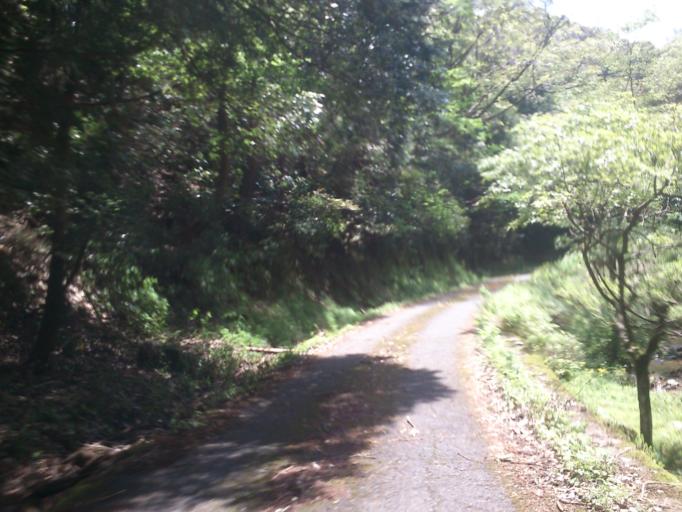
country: JP
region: Kyoto
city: Miyazu
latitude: 35.7034
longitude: 135.1200
